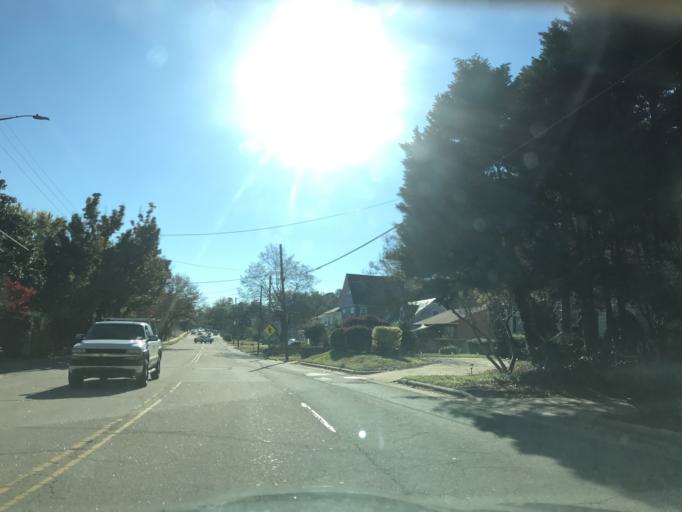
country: US
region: North Carolina
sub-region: Wake County
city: Raleigh
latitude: 35.7975
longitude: -78.6295
